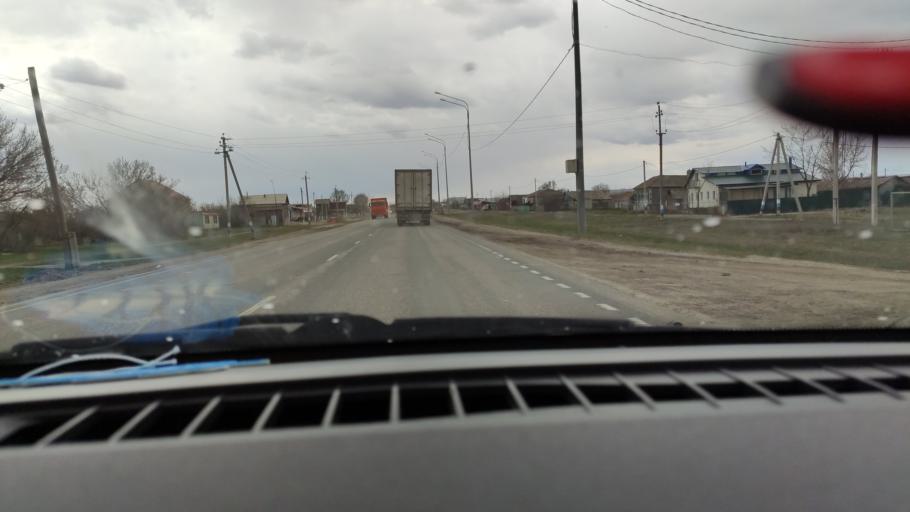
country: RU
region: Saratov
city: Sinodskoye
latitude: 51.9871
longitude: 46.6648
